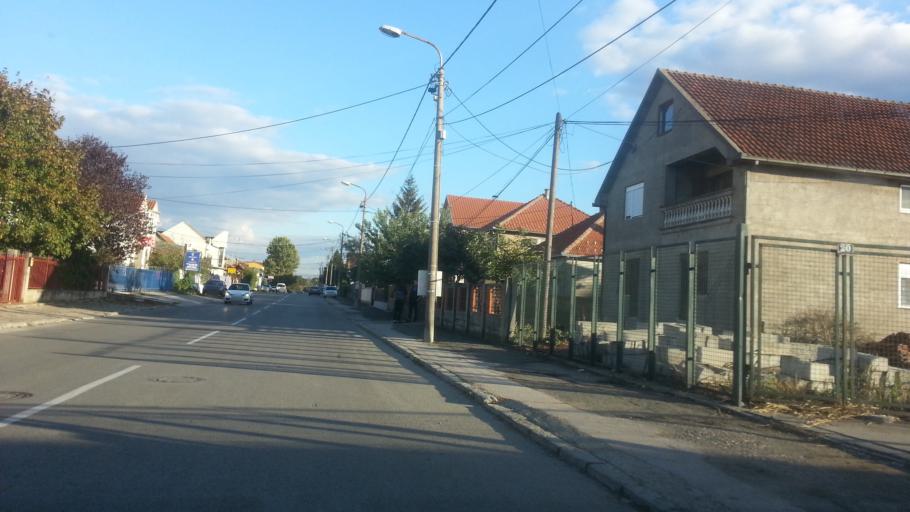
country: RS
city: Novi Banovci
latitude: 44.9057
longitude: 20.2813
